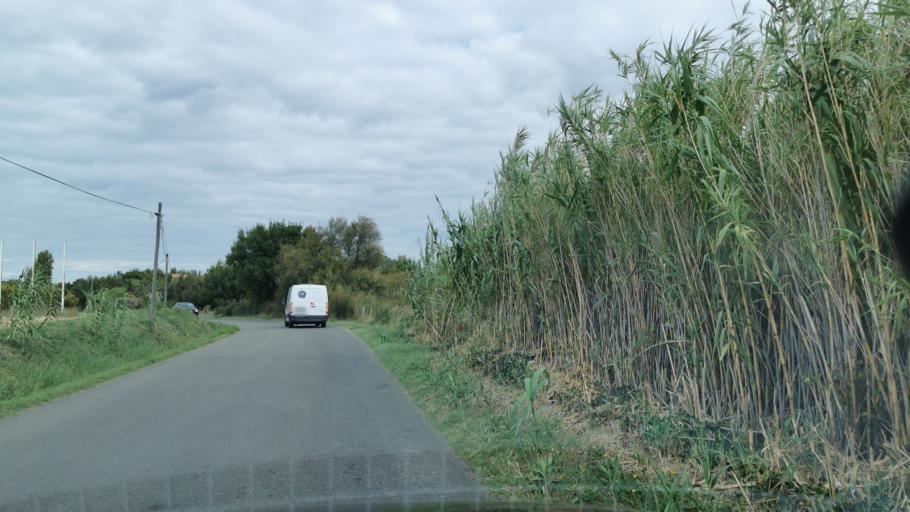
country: FR
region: Languedoc-Roussillon
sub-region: Departement de l'Herault
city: Lespignan
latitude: 43.2286
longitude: 3.1941
